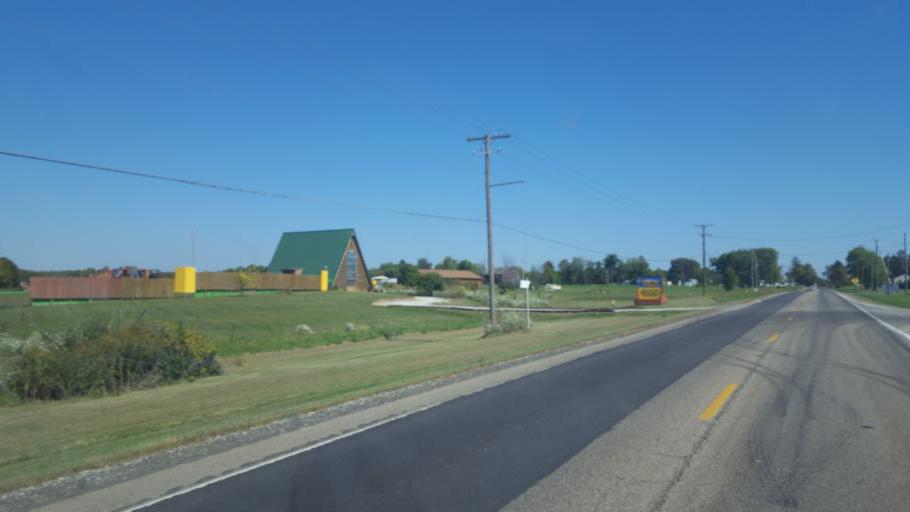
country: US
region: Ohio
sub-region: Crawford County
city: Galion
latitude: 40.6671
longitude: -82.8533
